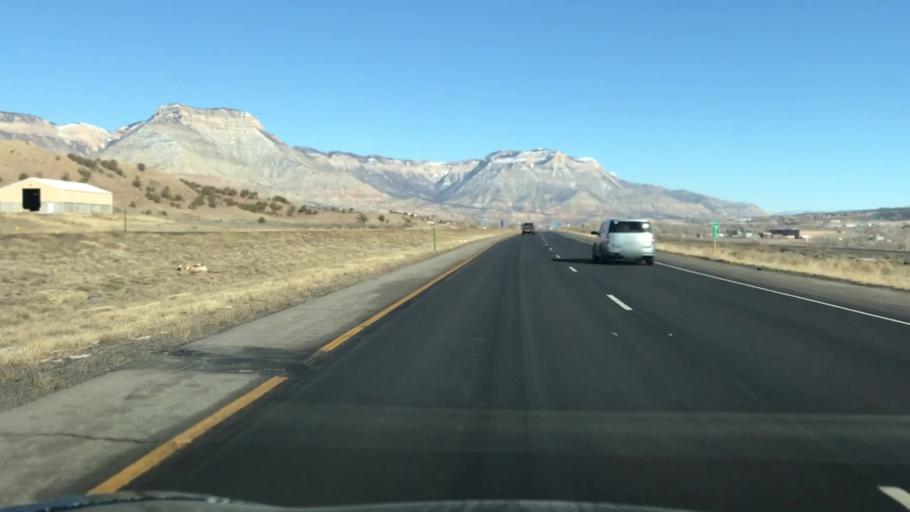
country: US
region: Colorado
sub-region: Garfield County
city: Parachute
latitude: 39.4369
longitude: -108.0671
